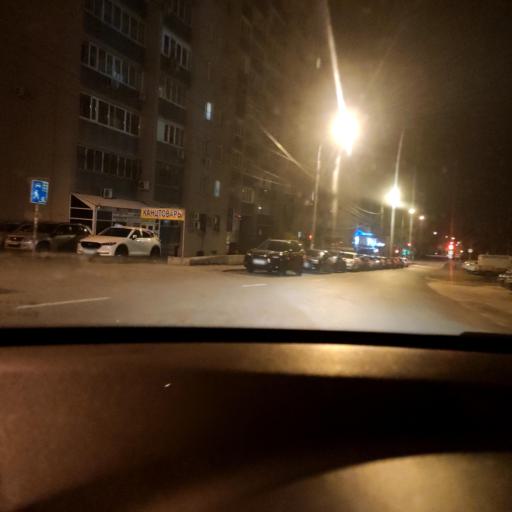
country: RU
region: Samara
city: Samara
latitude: 53.2081
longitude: 50.2209
